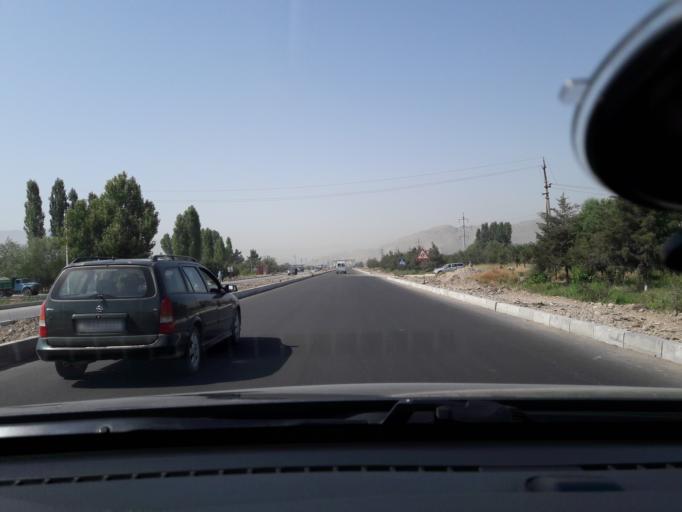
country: TJ
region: Dushanbe
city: Boshkengash
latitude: 38.4817
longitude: 68.7471
